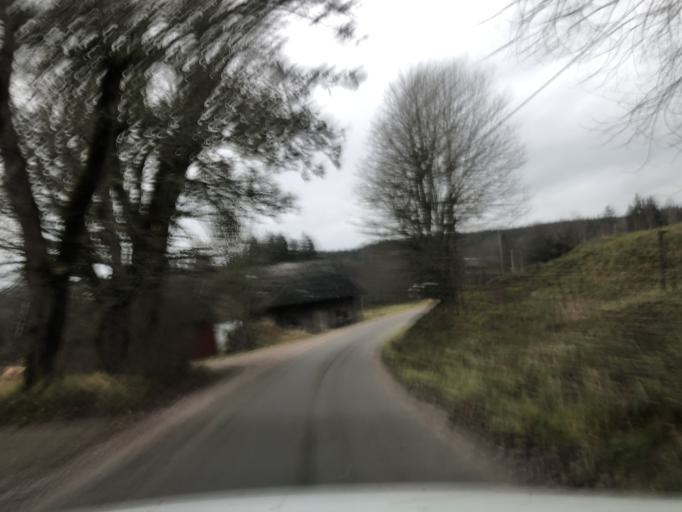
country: SE
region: Vaestra Goetaland
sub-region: Ulricehamns Kommun
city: Ulricehamn
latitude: 57.8613
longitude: 13.5752
